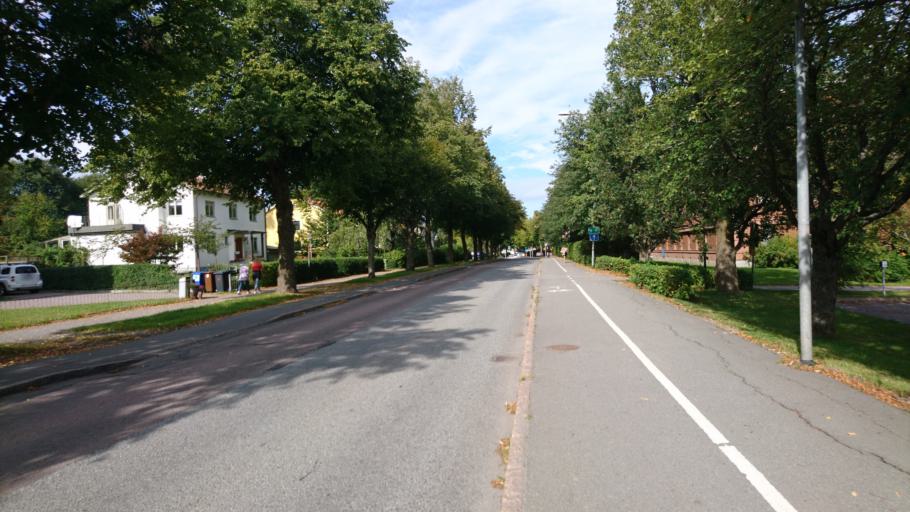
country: SE
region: Uppsala
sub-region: Uppsala Kommun
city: Uppsala
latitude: 59.8486
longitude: 17.6222
